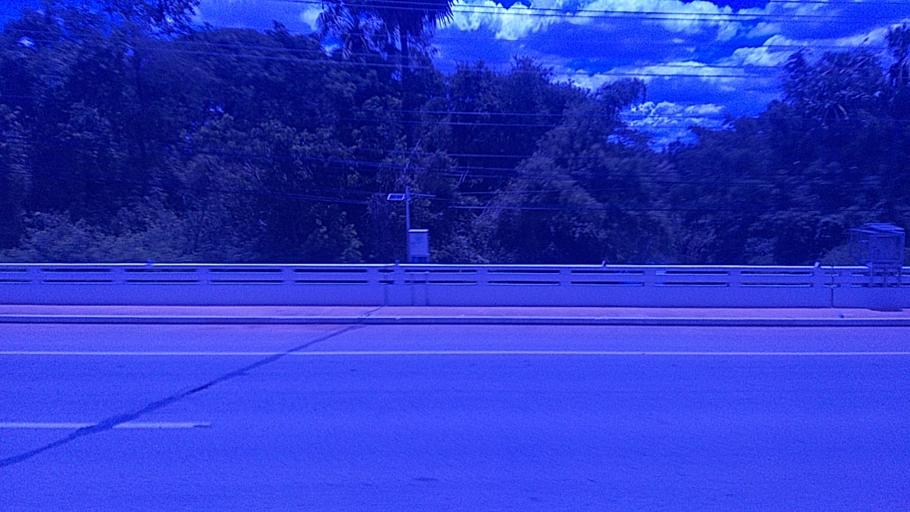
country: TH
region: Chaiyaphum
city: Noen Sa-nga
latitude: 15.6814
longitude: 102.0096
